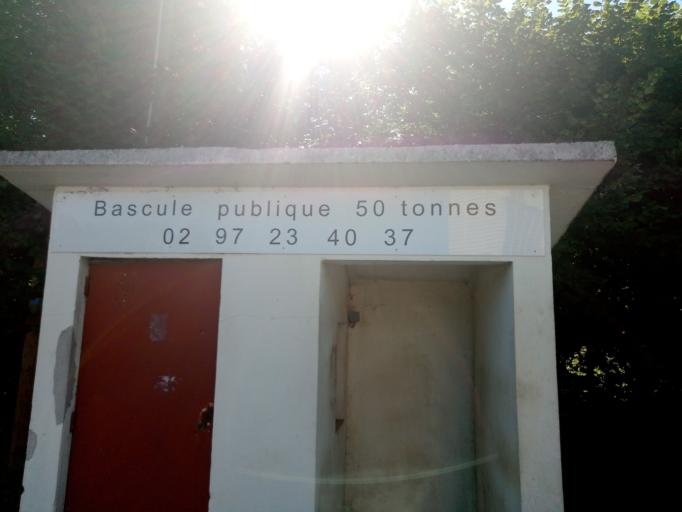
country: FR
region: Brittany
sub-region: Departement du Morbihan
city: Gourin
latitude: 48.1492
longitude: -3.6056
